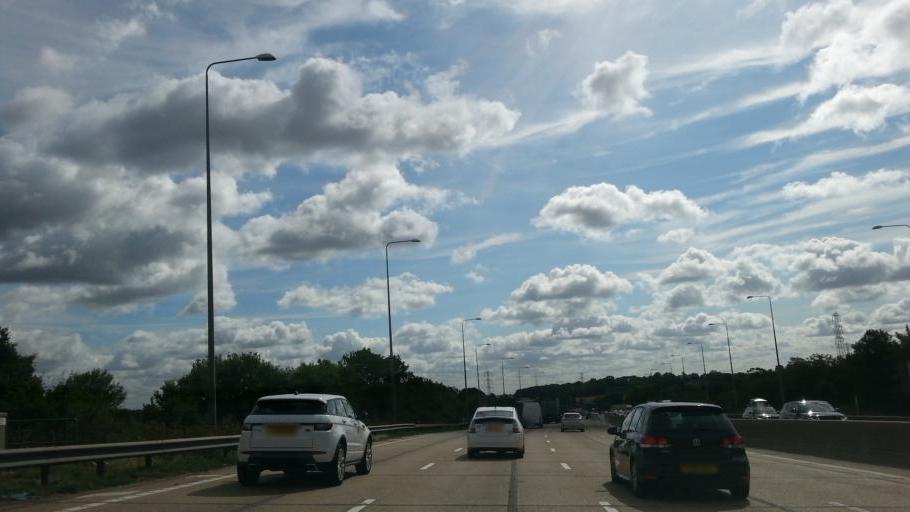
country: GB
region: England
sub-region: Hertfordshire
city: Potters Bar
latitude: 51.6877
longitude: -0.1608
